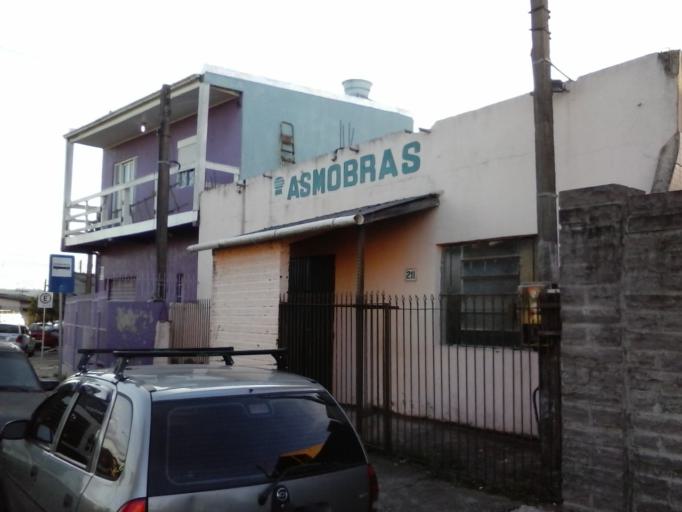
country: BR
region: Rio Grande do Sul
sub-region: Porto Alegre
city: Porto Alegre
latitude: -30.0447
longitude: -51.1497
